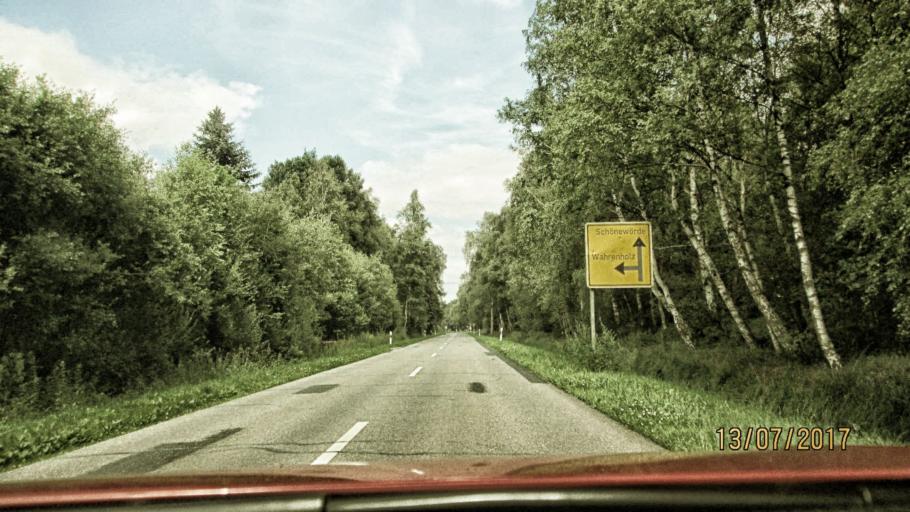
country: DE
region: Lower Saxony
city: Sassenburg
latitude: 52.5617
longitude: 10.6257
